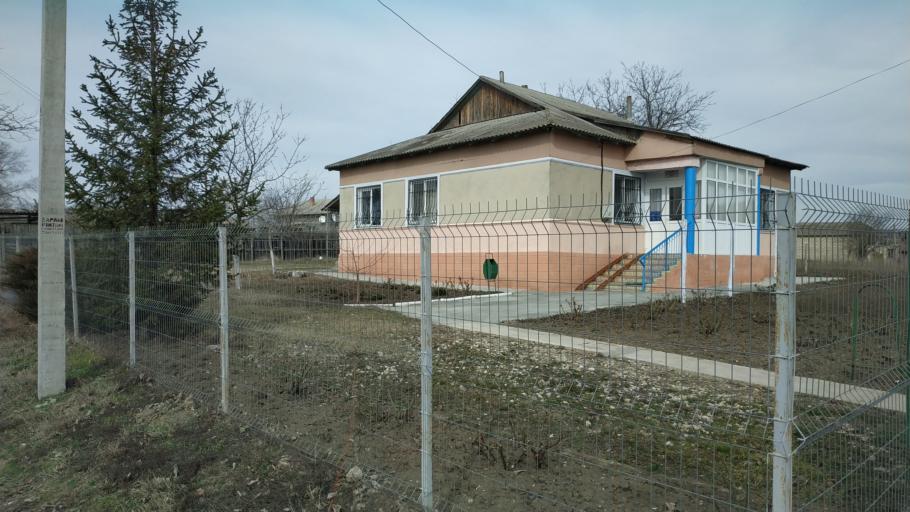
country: MD
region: Hincesti
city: Dancu
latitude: 46.8613
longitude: 28.2486
